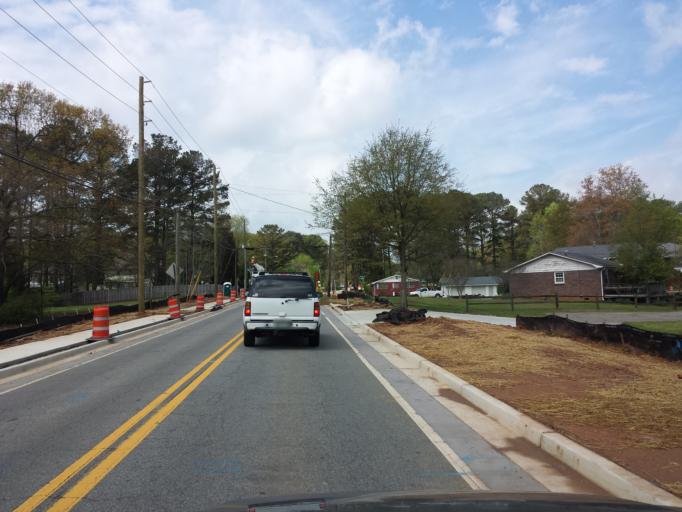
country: US
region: Georgia
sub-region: Cherokee County
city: Woodstock
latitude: 34.0317
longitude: -84.4975
